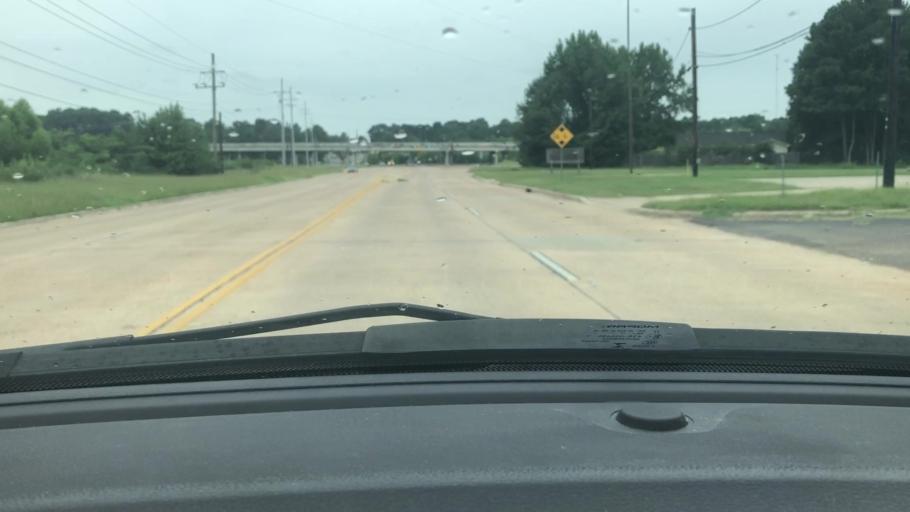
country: US
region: Texas
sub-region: Bowie County
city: Wake Village
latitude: 33.4332
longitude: -94.0936
